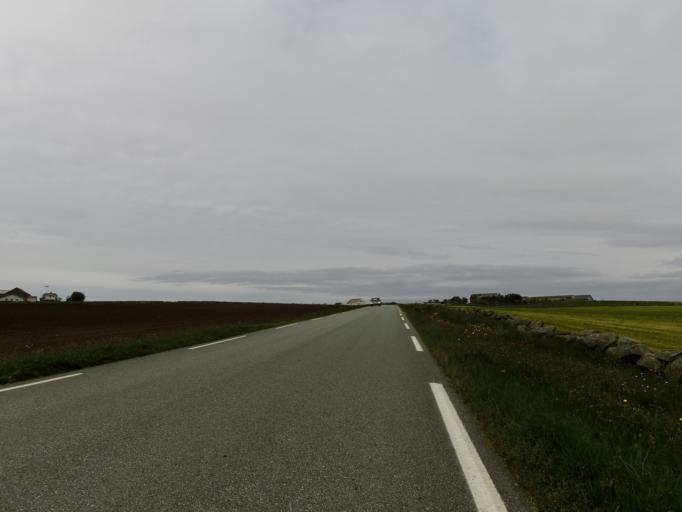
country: NO
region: Rogaland
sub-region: Klepp
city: Kleppe
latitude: 58.8155
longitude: 5.5766
